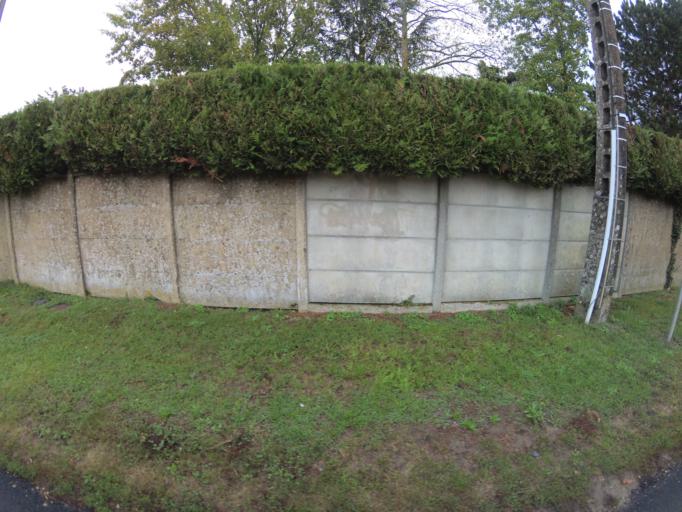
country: FR
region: Ile-de-France
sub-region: Departement de Seine-et-Marne
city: Chanteloup-en-Brie
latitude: 48.8419
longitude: 2.7514
